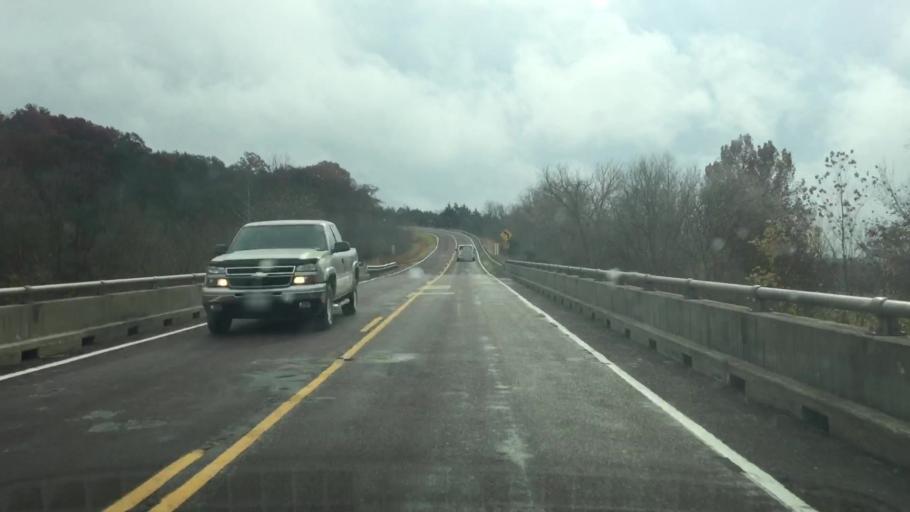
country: US
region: Missouri
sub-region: Callaway County
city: Fulton
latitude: 38.7798
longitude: -91.8502
